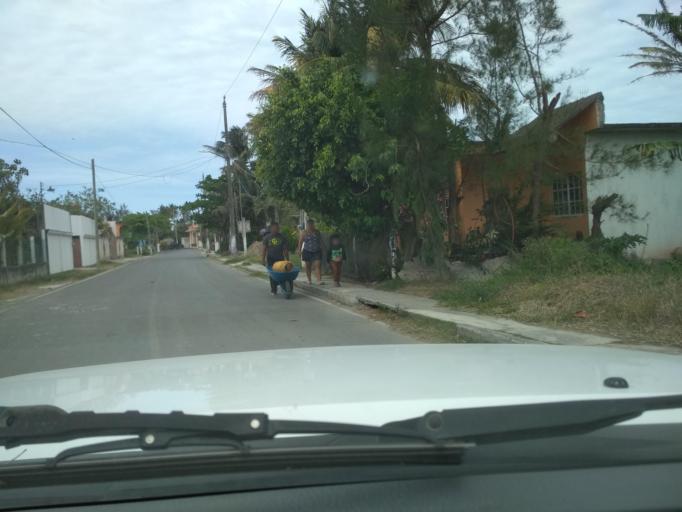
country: MX
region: Veracruz
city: Anton Lizardo
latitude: 19.0360
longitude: -95.9698
